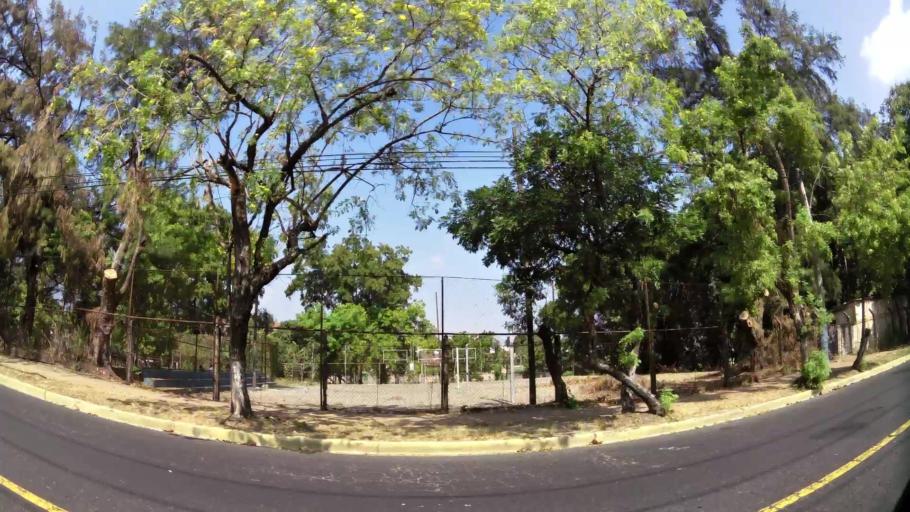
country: SV
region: San Salvador
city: San Salvador
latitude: 13.6971
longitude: -89.2121
